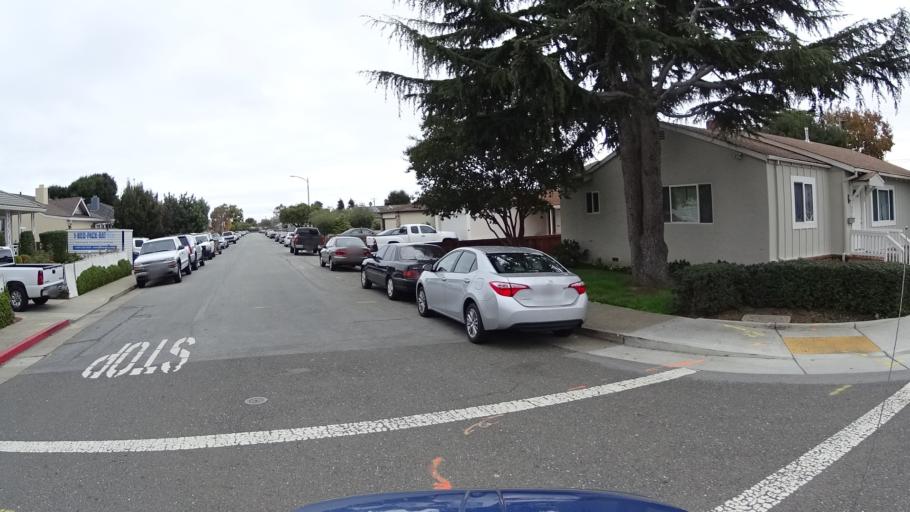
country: US
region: California
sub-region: San Mateo County
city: Belmont
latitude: 37.5338
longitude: -122.2928
